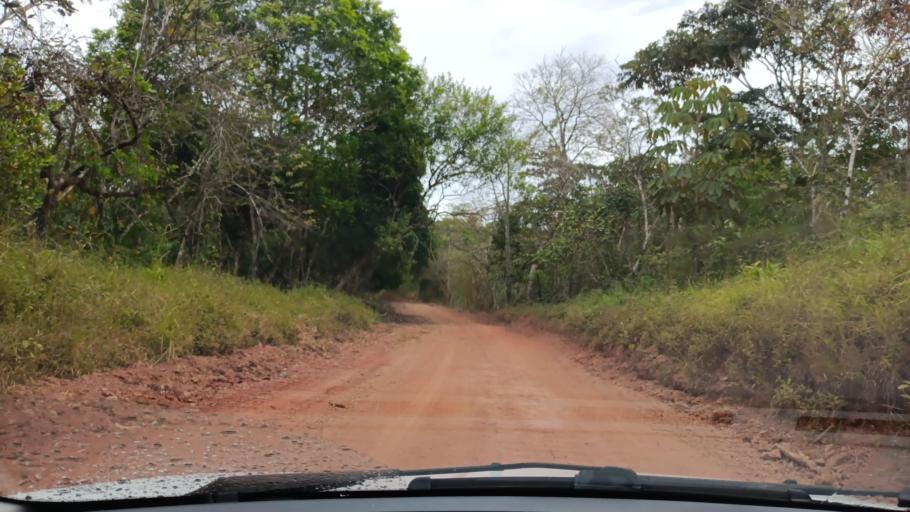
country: PA
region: Panama
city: La Cabima
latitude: 9.1282
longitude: -79.5055
